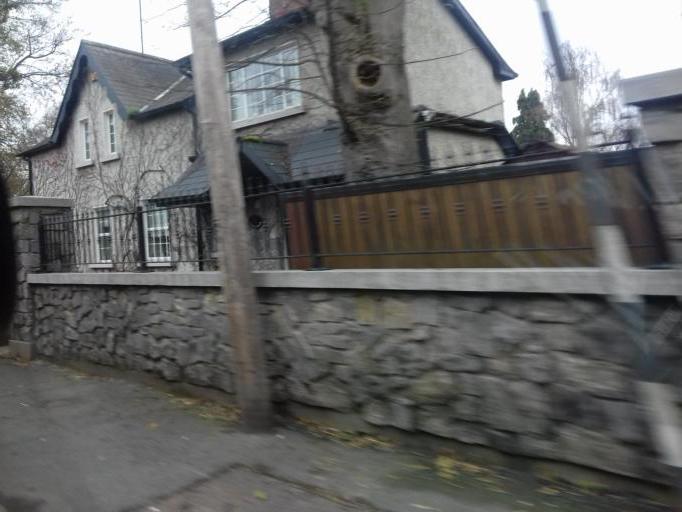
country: IE
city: Darndale
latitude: 53.4251
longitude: -6.1750
